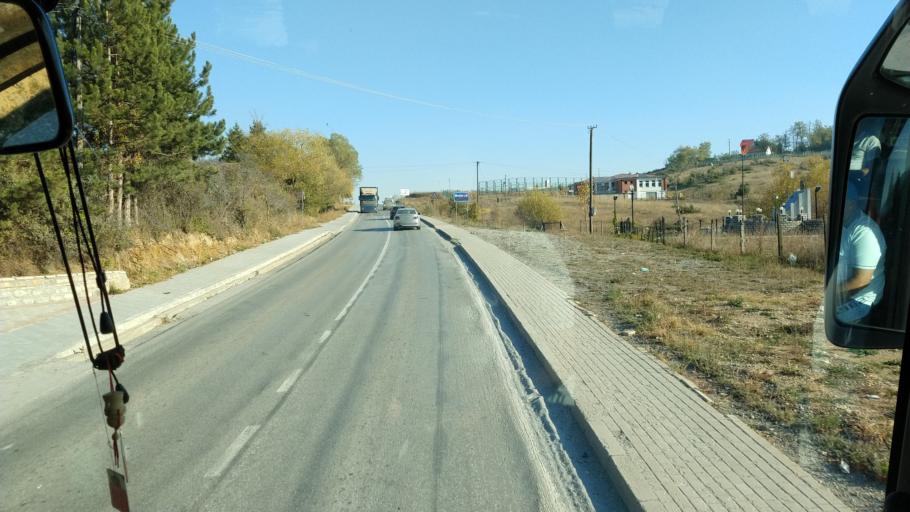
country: XK
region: Ferizaj
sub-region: Komuna e Shtimes
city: Shtime
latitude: 42.4385
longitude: 21.0195
